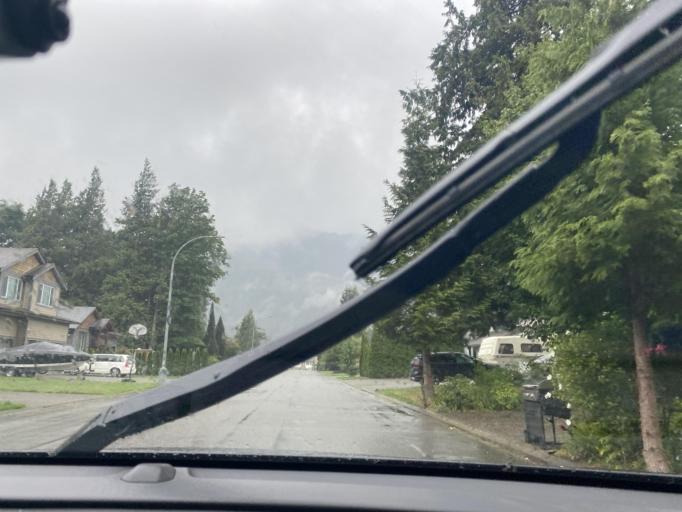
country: CA
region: British Columbia
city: Agassiz
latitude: 49.3002
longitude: -121.7733
